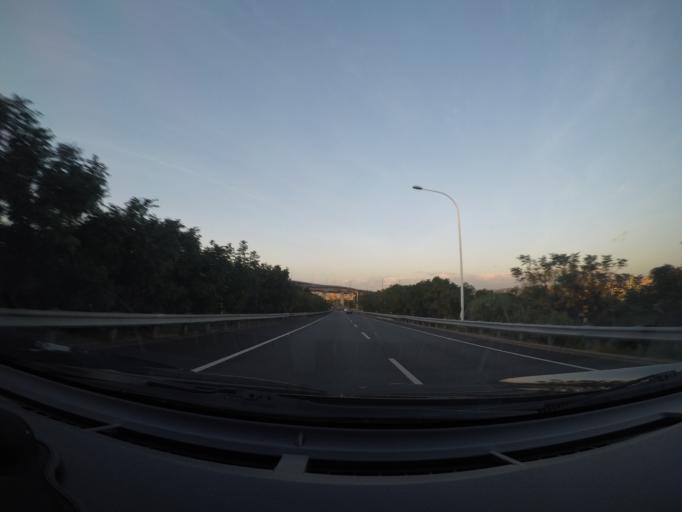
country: TW
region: Taiwan
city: Taoyuan City
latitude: 25.0191
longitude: 121.2768
